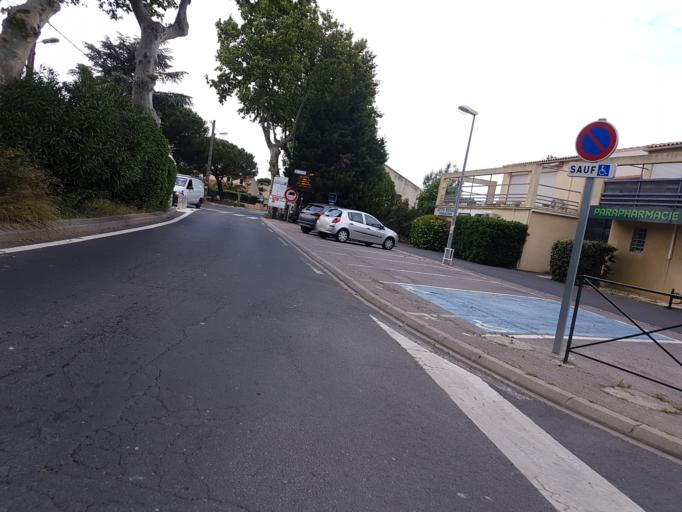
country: FR
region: Languedoc-Roussillon
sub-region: Departement de l'Herault
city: Cers
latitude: 43.3202
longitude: 3.3034
